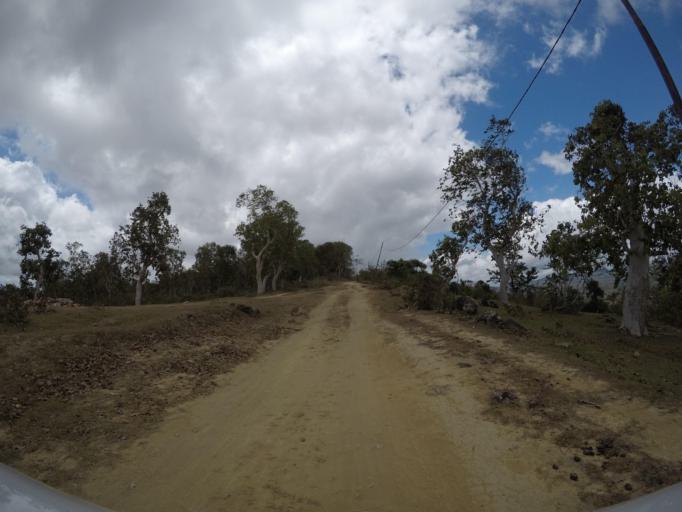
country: TL
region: Lautem
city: Lospalos
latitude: -8.5567
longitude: 126.8343
